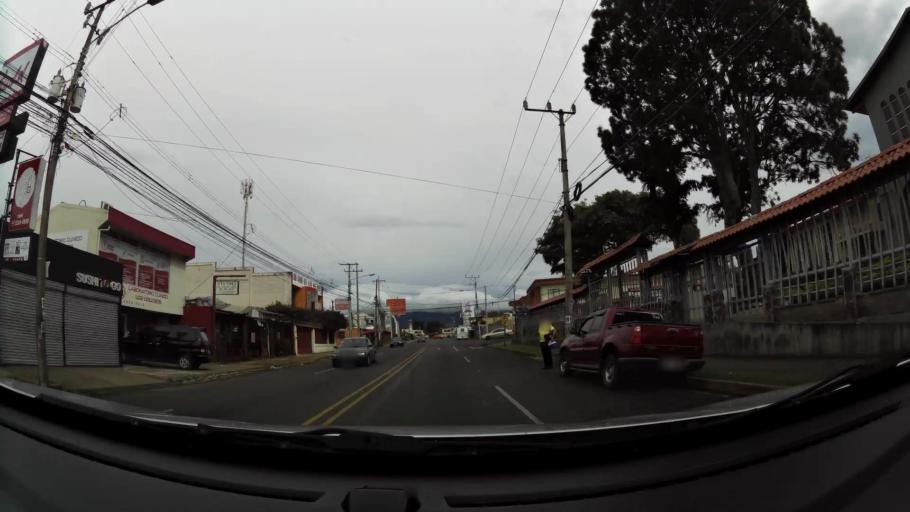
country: CR
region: San Jose
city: San Vicente de Moravia
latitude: 9.9605
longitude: -84.0549
